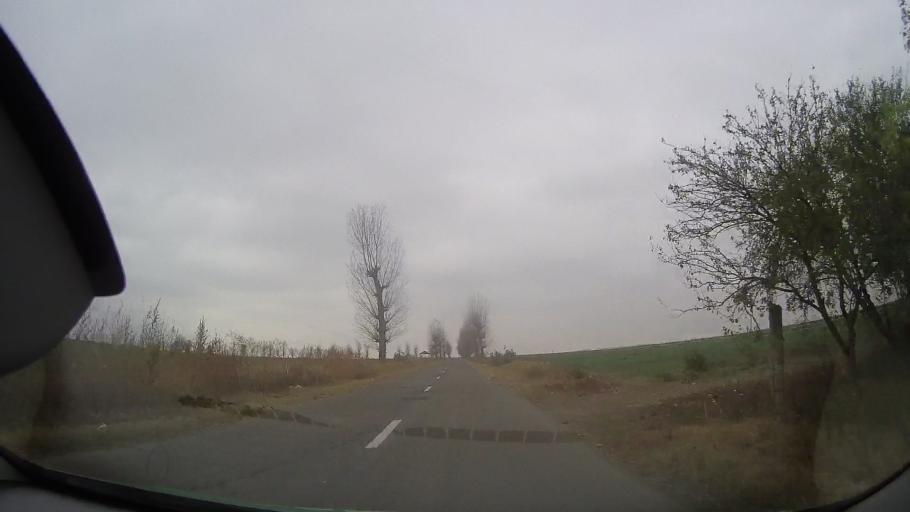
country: RO
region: Ialomita
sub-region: Comuna Grindu
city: Grindu
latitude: 44.7712
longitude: 26.8937
